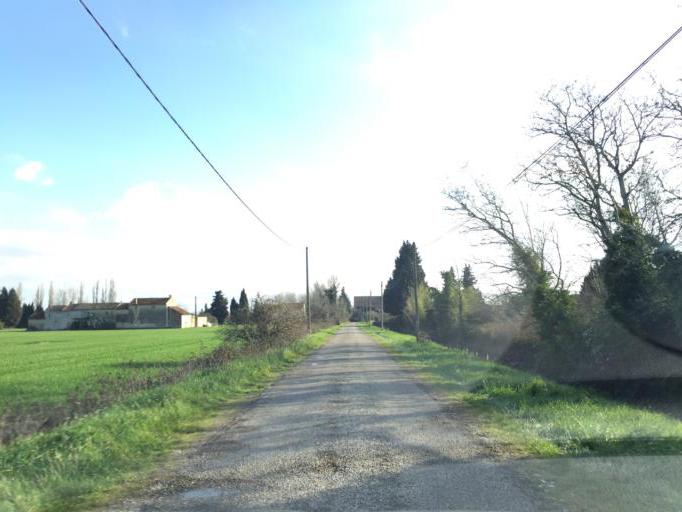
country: FR
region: Provence-Alpes-Cote d'Azur
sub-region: Departement du Vaucluse
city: Orange
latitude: 44.1389
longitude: 4.8262
